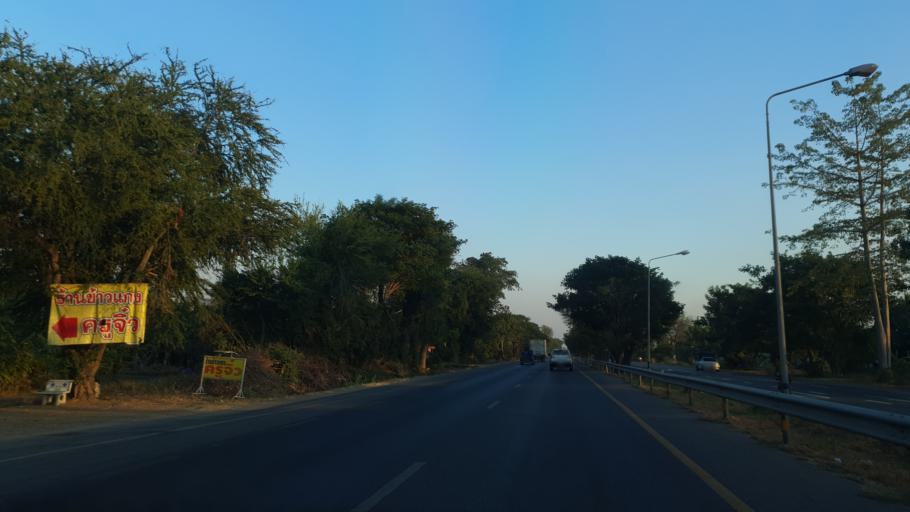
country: TH
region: Kamphaeng Phet
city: Khanu Woralaksaburi
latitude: 15.9598
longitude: 99.8436
